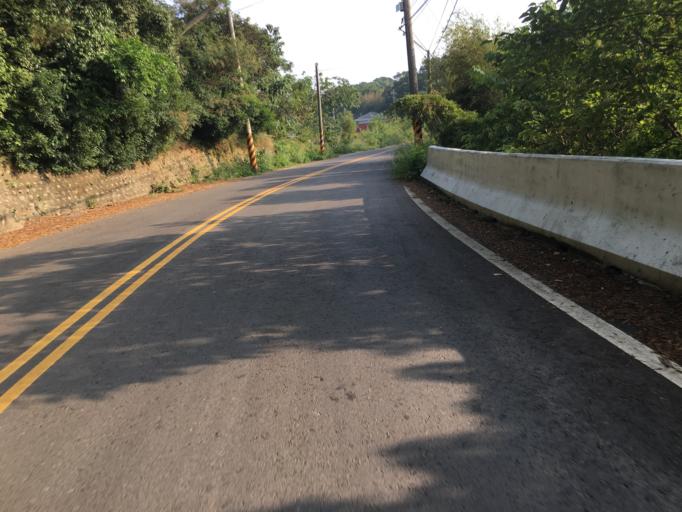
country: TW
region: Taiwan
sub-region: Hsinchu
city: Hsinchu
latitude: 24.7516
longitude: 121.0321
